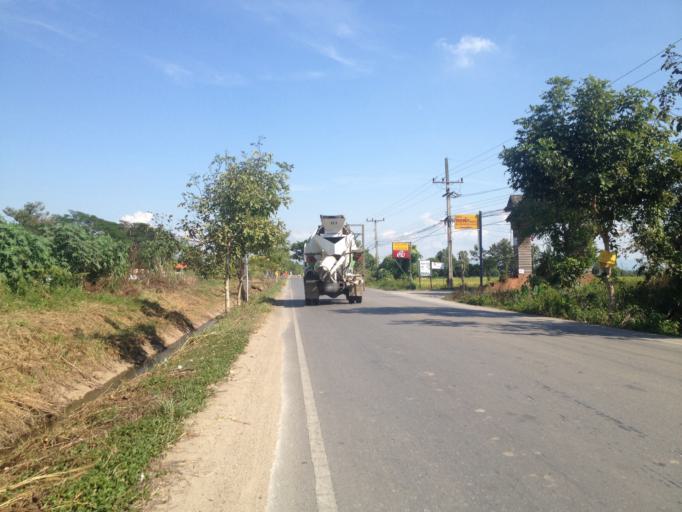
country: TH
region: Chiang Mai
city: Hang Dong
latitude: 18.6891
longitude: 98.9532
